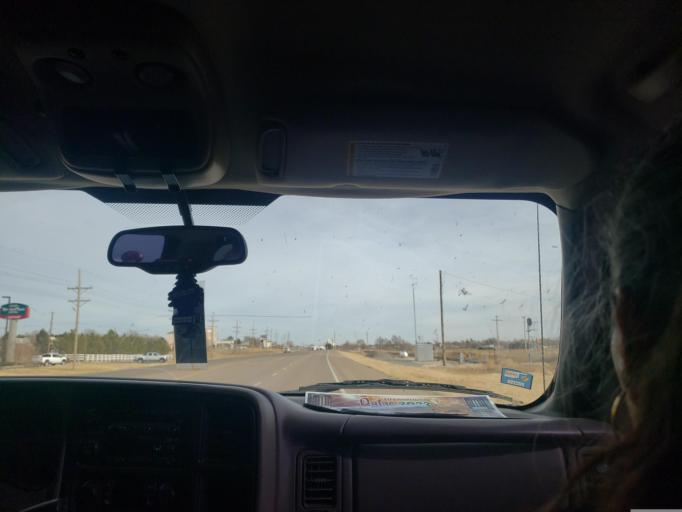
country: US
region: Kansas
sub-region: Ford County
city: Dodge City
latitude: 37.7546
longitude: -100.0573
